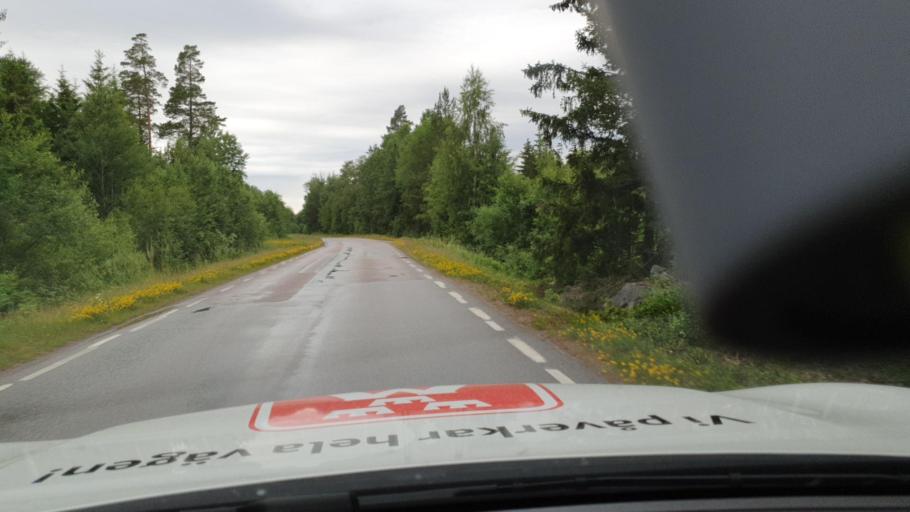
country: SE
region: Vaestra Goetaland
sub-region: Toreboda Kommun
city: Toereboda
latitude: 58.8283
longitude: 13.9997
